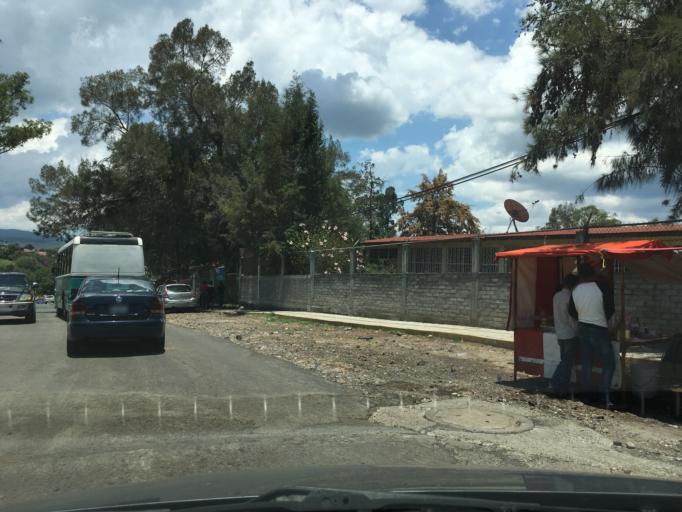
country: MX
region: Michoacan
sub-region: Morelia
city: La Mintzita (Piedra Dura)
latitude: 19.5965
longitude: -101.2916
